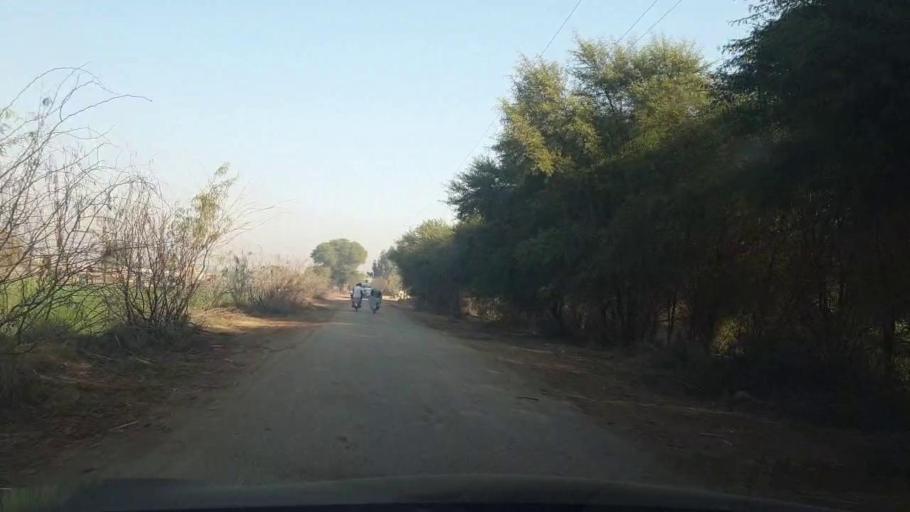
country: PK
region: Sindh
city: Mirpur Mathelo
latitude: 28.0737
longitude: 69.4678
